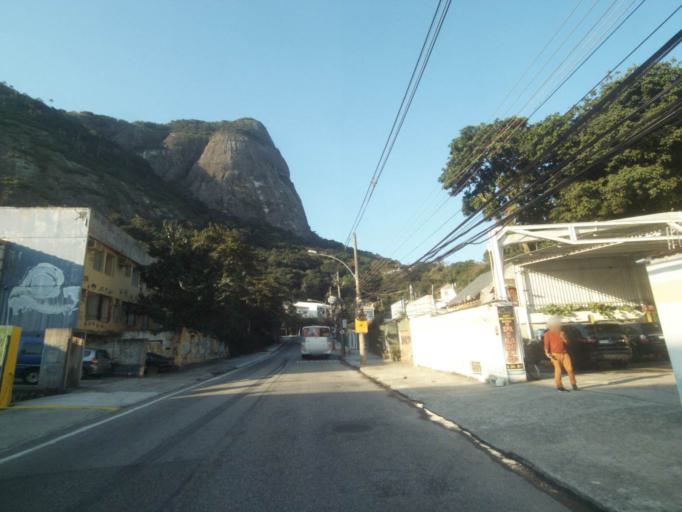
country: BR
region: Rio de Janeiro
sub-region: Rio De Janeiro
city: Rio de Janeiro
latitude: -23.0085
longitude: -43.2935
